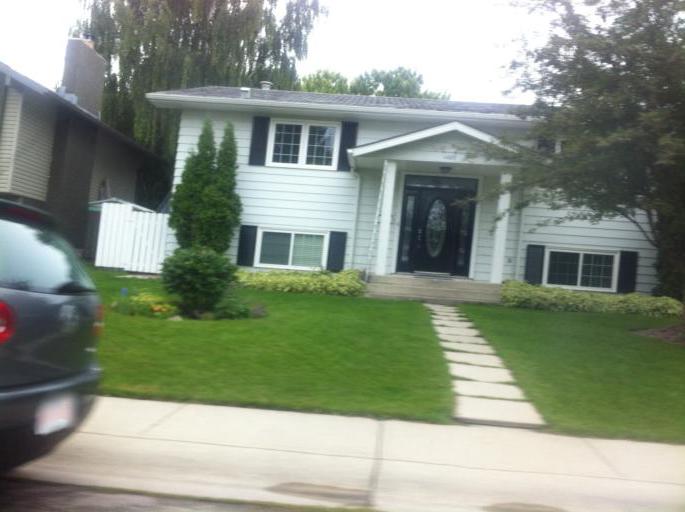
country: CA
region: Alberta
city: Calgary
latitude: 50.9357
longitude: -114.0365
